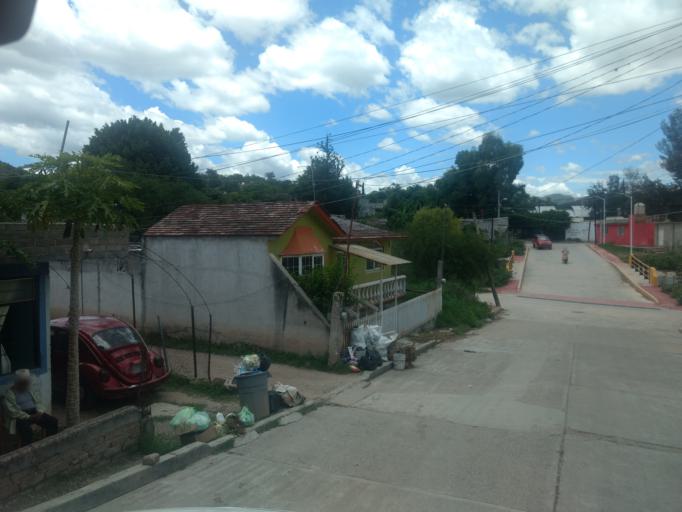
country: MX
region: Oaxaca
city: Ciudad de Huajuapam de Leon
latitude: 17.8142
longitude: -97.7690
